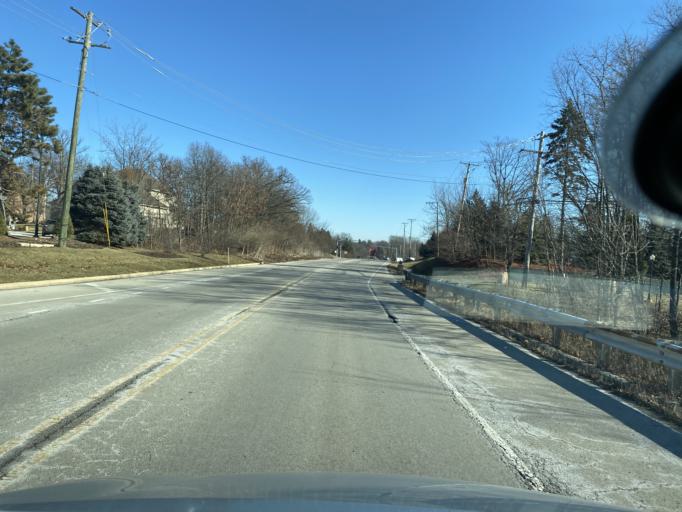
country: US
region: Illinois
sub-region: Cook County
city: Lemont
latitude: 41.6494
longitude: -87.9912
